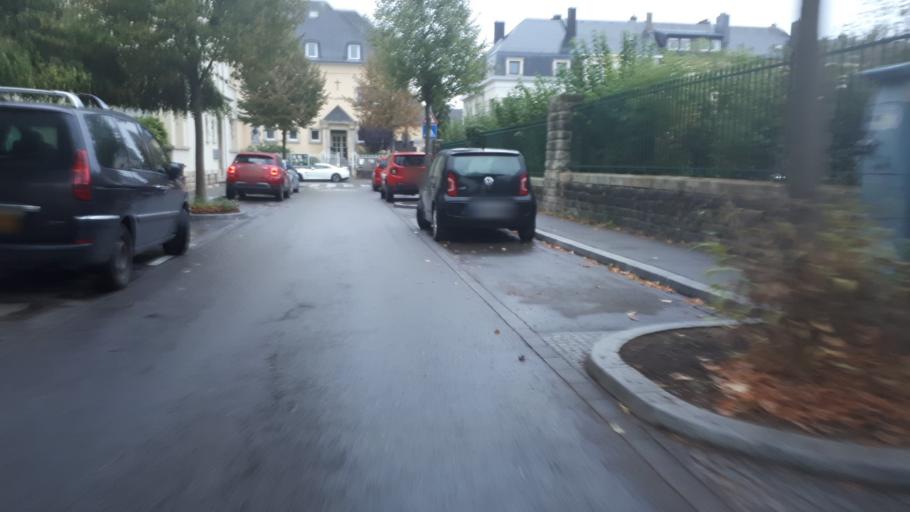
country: LU
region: Luxembourg
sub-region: Canton de Luxembourg
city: Luxembourg
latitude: 49.6107
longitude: 6.1154
